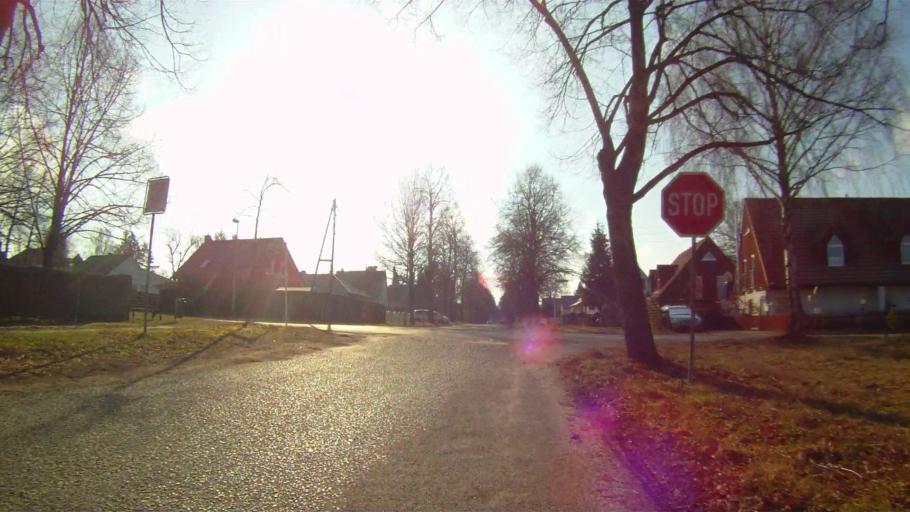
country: DE
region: Brandenburg
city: Schoneiche
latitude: 52.4737
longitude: 13.7012
